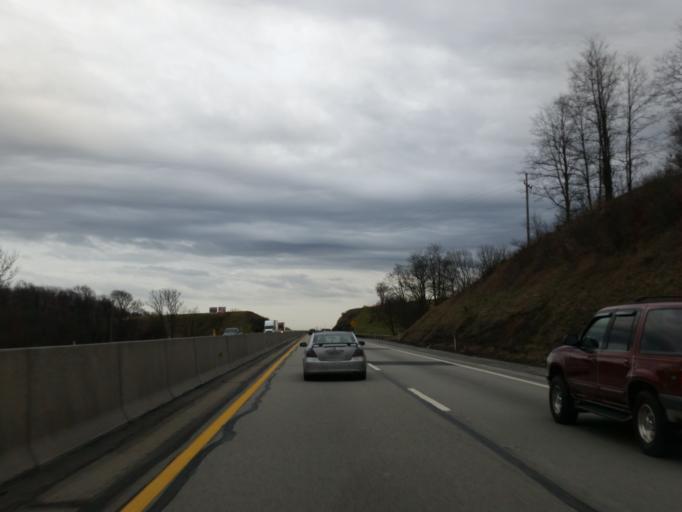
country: US
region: Pennsylvania
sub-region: Somerset County
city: Somerset
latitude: 40.0499
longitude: -79.1242
